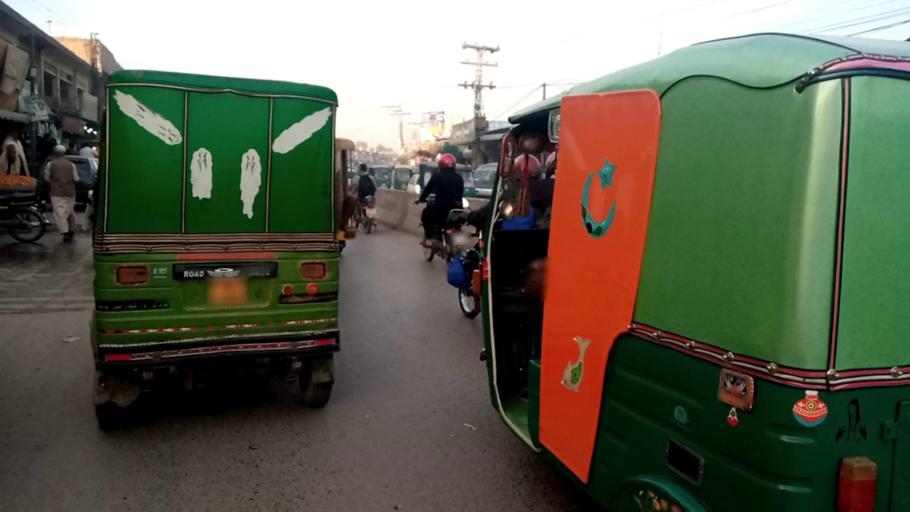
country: PK
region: Khyber Pakhtunkhwa
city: Peshawar
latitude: 34.0294
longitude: 71.5758
